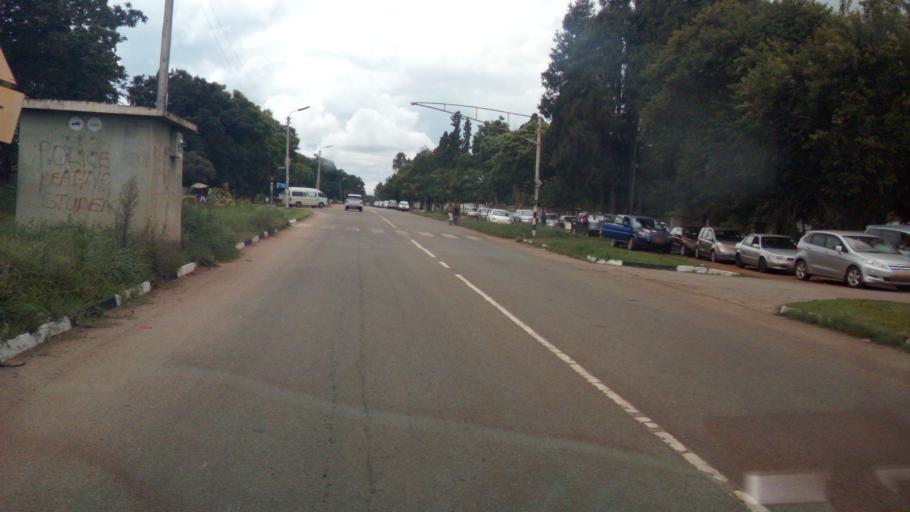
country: ZW
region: Harare
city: Harare
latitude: -17.7512
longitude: 31.0142
